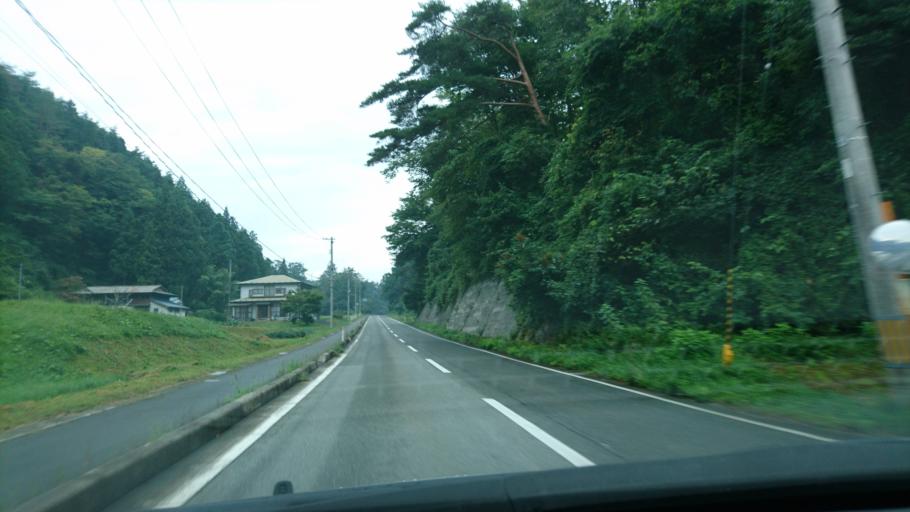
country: JP
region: Iwate
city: Ichinoseki
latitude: 39.0126
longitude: 141.2600
